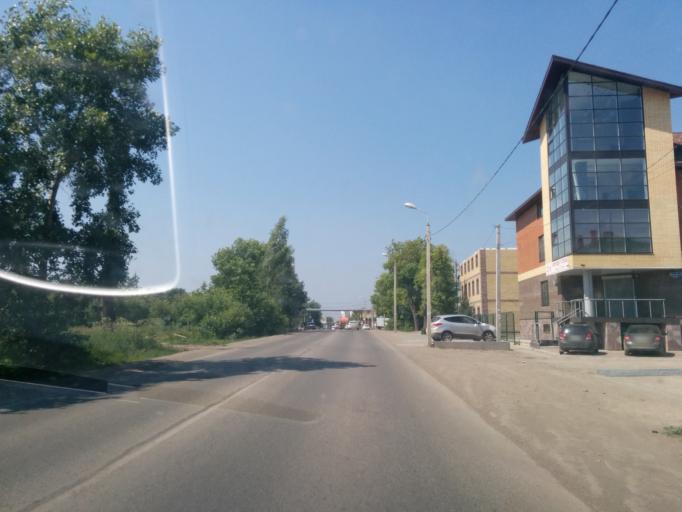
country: RU
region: Perm
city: Perm
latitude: 57.9875
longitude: 56.3033
